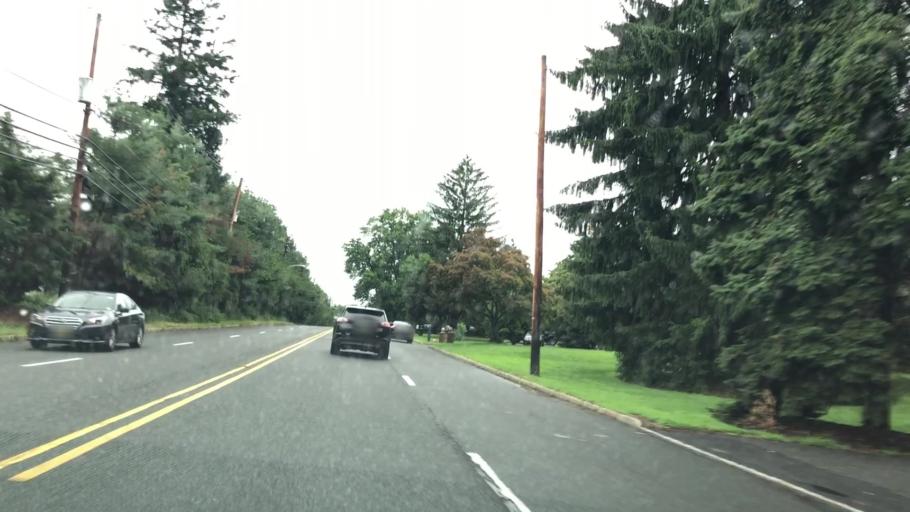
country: US
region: New Jersey
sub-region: Morris County
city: Hanover
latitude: 40.8096
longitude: -74.3617
